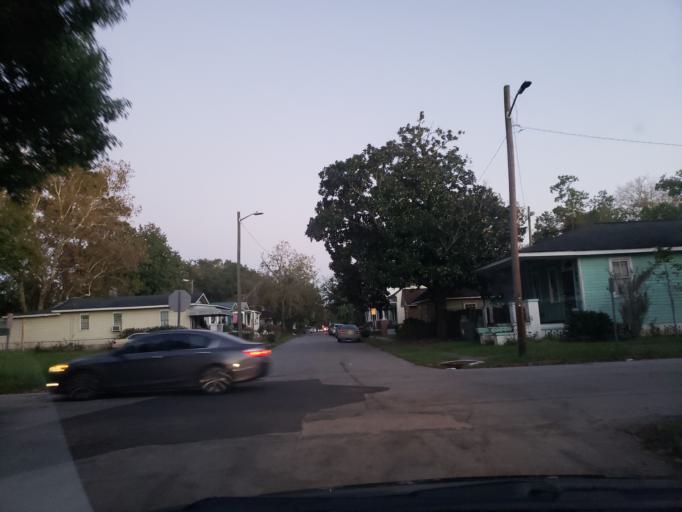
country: US
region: Georgia
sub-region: Chatham County
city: Savannah
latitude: 32.0523
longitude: -81.0866
